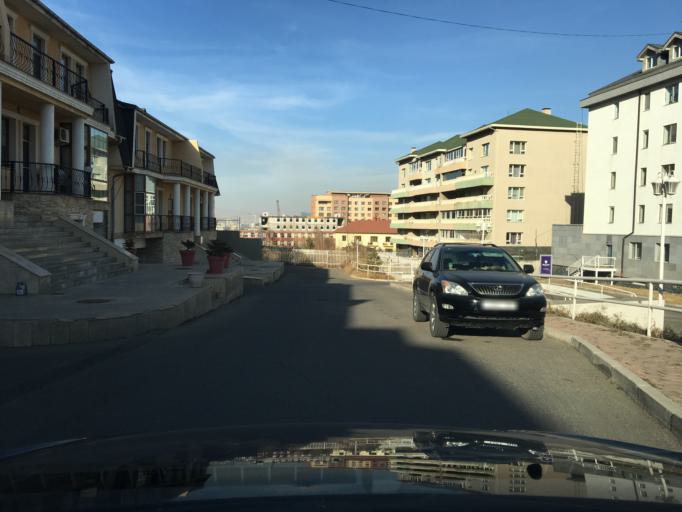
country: MN
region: Ulaanbaatar
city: Ulaanbaatar
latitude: 47.8787
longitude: 106.9092
